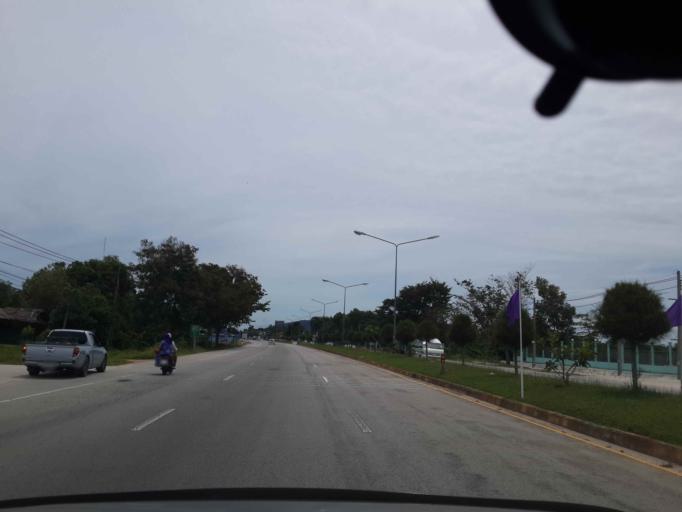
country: TH
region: Narathiwat
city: Narathiwat
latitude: 6.4089
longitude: 101.7964
